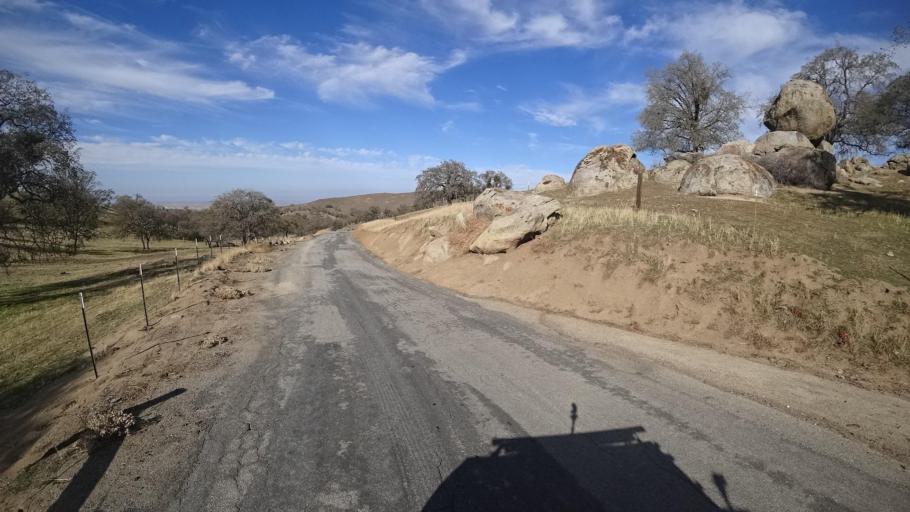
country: US
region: California
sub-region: Kern County
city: Oildale
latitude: 35.5934
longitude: -118.8257
